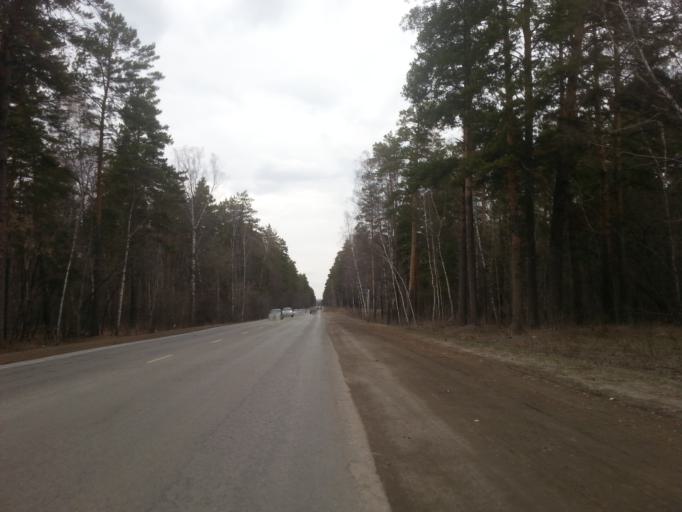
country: RU
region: Altai Krai
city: Yuzhnyy
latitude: 53.2761
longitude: 83.7204
